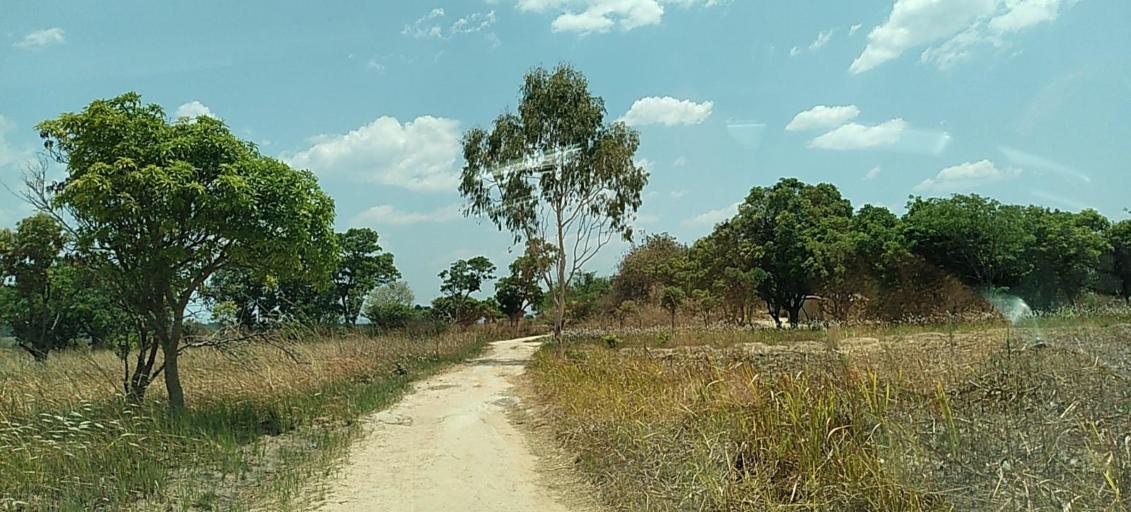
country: ZM
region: Copperbelt
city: Chililabombwe
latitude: -12.4710
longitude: 27.6657
